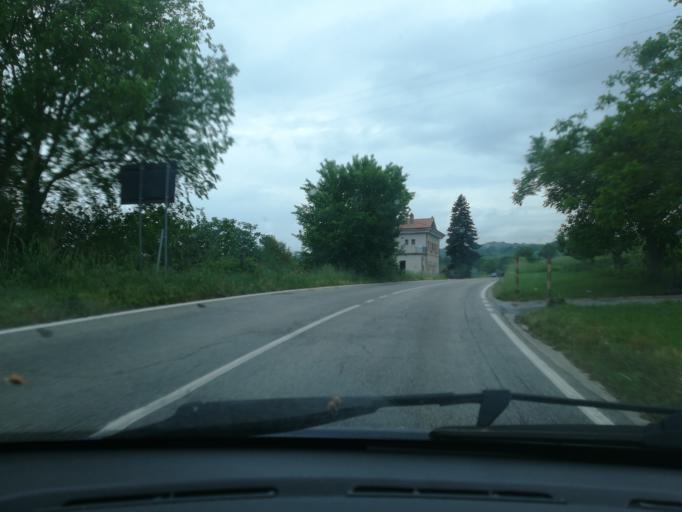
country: IT
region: The Marches
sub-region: Provincia di Macerata
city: Tolentino
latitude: 43.2647
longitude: 13.2505
